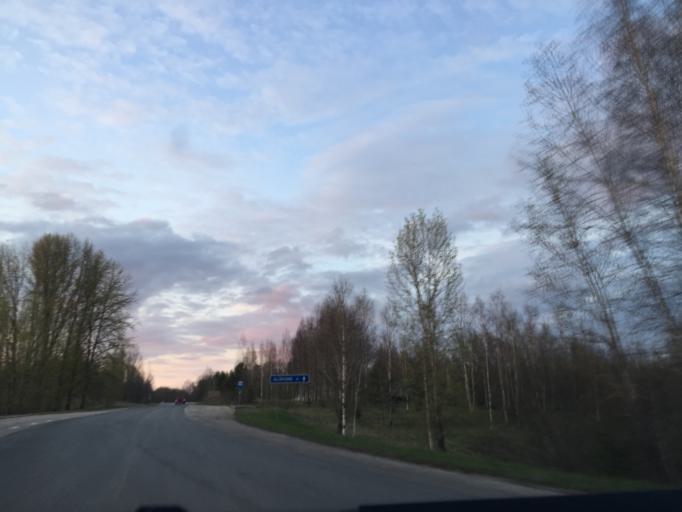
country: LV
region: Aluksnes Rajons
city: Aluksne
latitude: 57.3921
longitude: 27.0445
